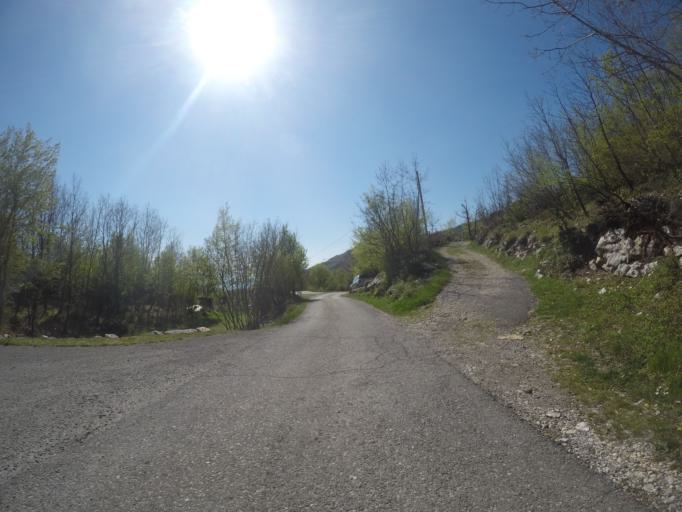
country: ME
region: Danilovgrad
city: Danilovgrad
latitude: 42.5177
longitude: 19.0523
